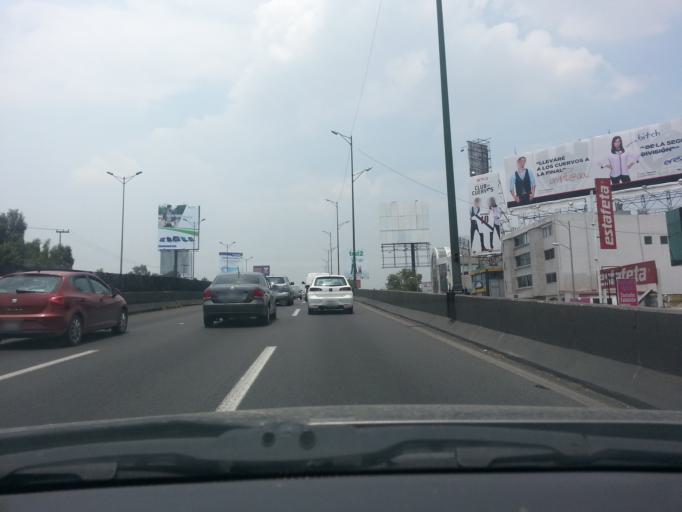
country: MX
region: Mexico
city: Vista Hermosa
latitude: 19.5029
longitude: -99.2367
